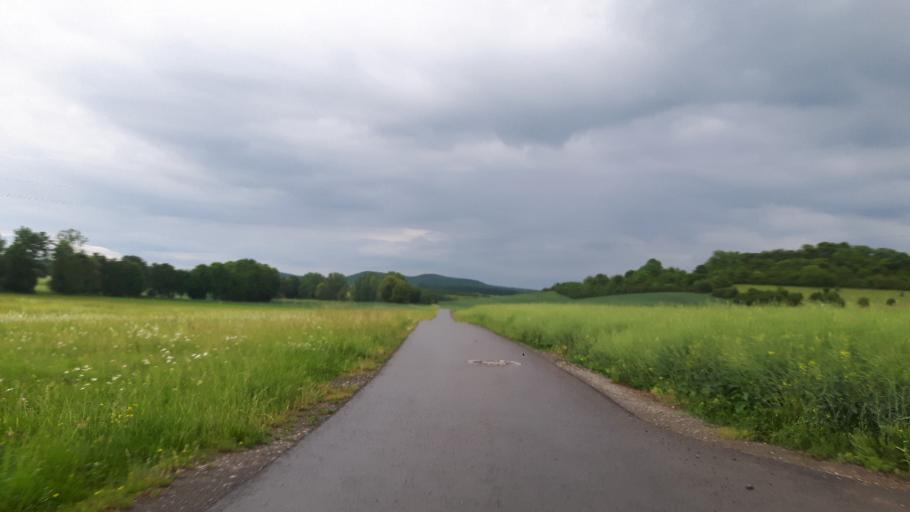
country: DE
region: Bavaria
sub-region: Regierungsbezirk Unterfranken
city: Stadtlauringen
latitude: 50.2024
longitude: 10.3698
